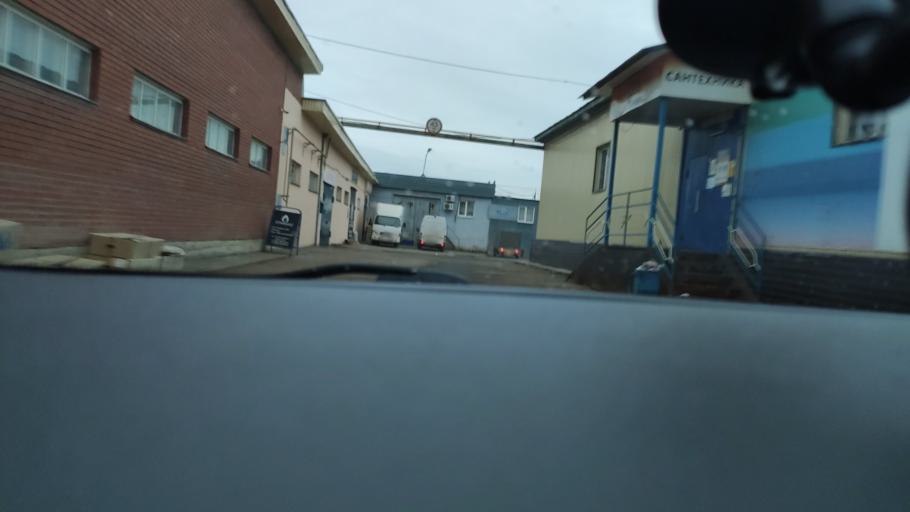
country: RU
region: Perm
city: Froly
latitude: 57.9556
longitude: 56.2244
